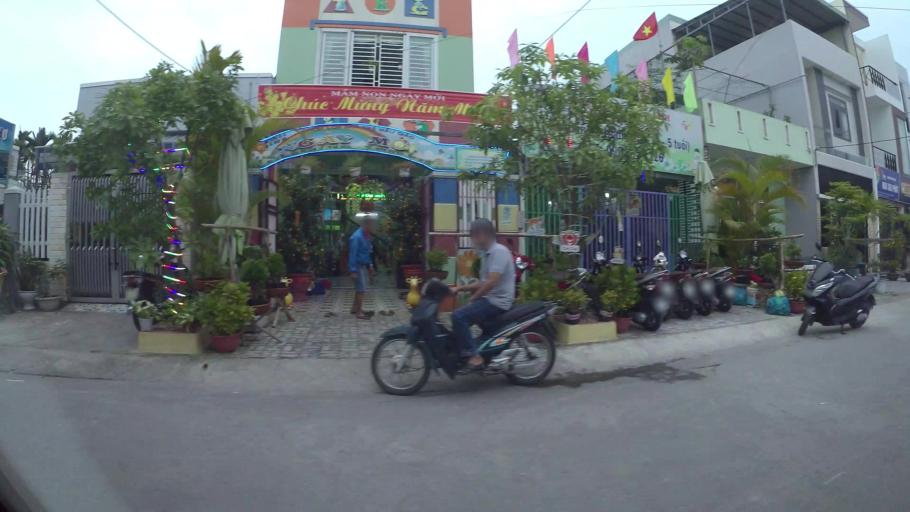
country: VN
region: Da Nang
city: Thanh Khe
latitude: 16.0464
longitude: 108.1803
